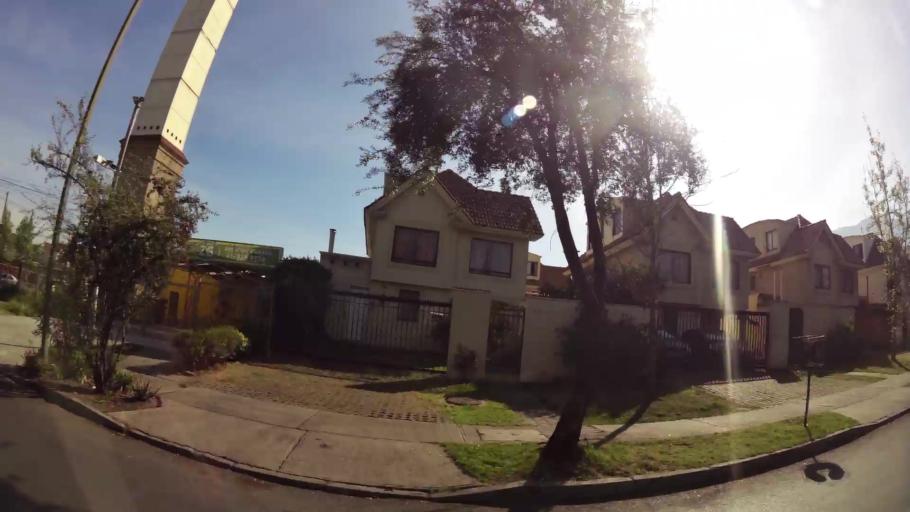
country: CL
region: Santiago Metropolitan
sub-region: Provincia de Santiago
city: Villa Presidente Frei, Nunoa, Santiago, Chile
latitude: -33.4836
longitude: -70.5463
